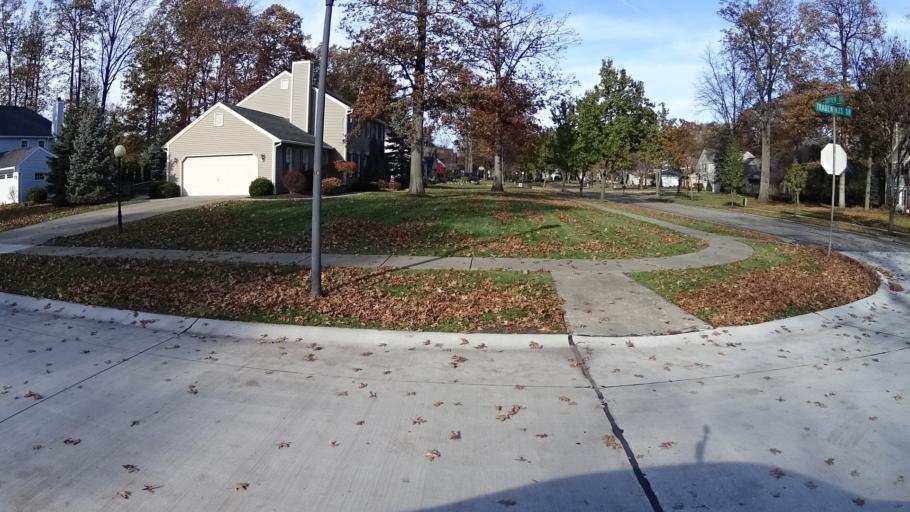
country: US
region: Ohio
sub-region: Lorain County
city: Avon Lake
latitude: 41.4985
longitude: -81.9749
